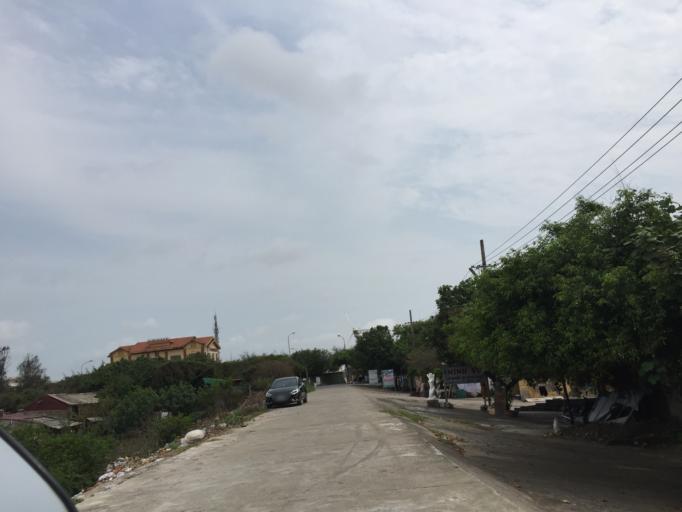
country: VN
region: Ninh Binh
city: Thi Tran Phat Diem
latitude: 20.0226
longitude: 106.2172
